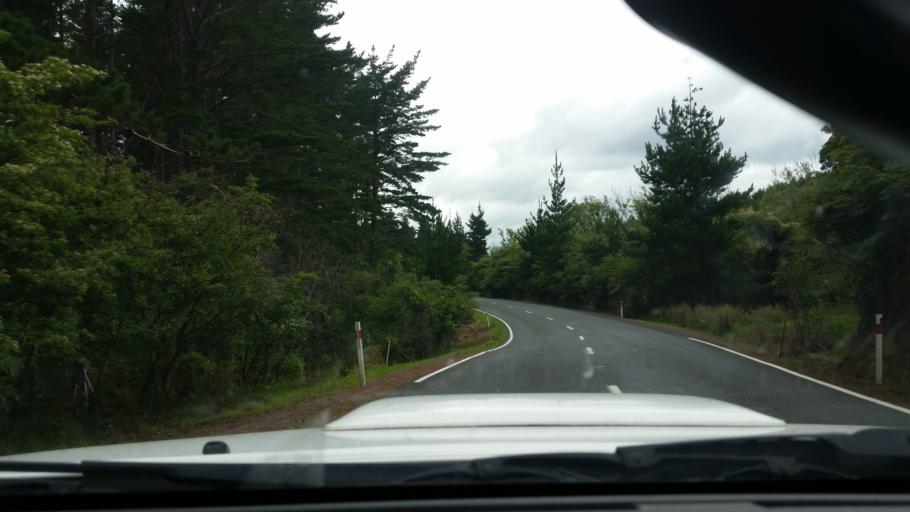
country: NZ
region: Northland
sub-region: Kaipara District
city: Dargaville
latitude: -35.7266
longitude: 173.8610
